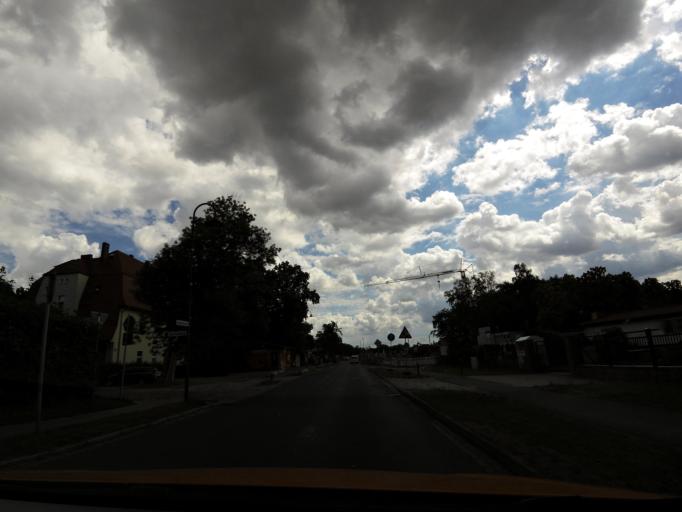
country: DE
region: Brandenburg
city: Rangsdorf
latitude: 52.3274
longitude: 13.4176
